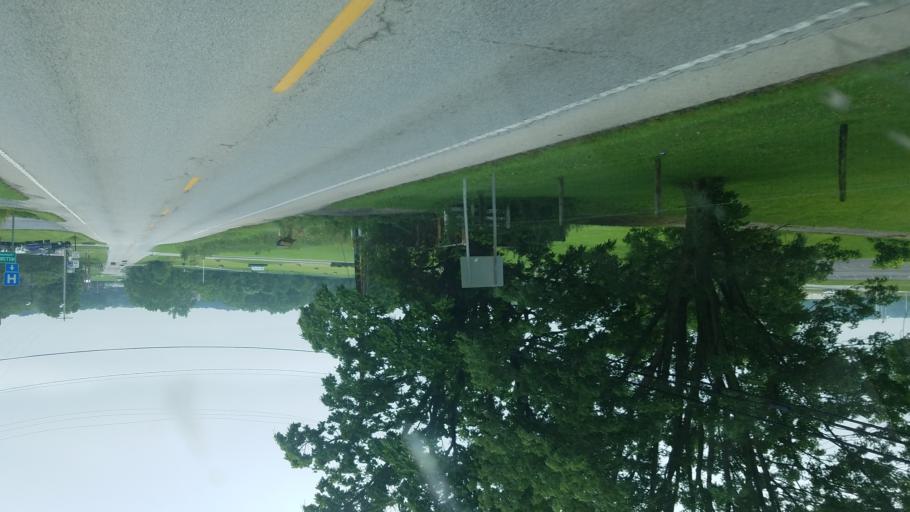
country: US
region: Ohio
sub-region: Highland County
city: Hillsboro
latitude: 39.2400
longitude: -83.6071
